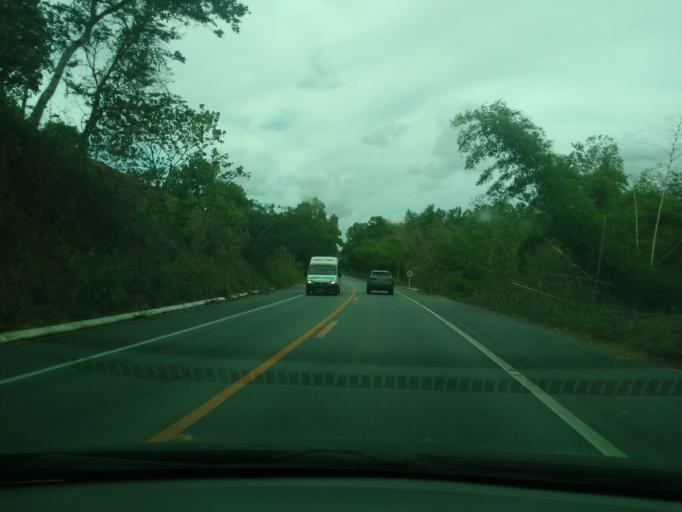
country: BR
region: Alagoas
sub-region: Murici
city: Murici
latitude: -9.2482
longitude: -35.9976
